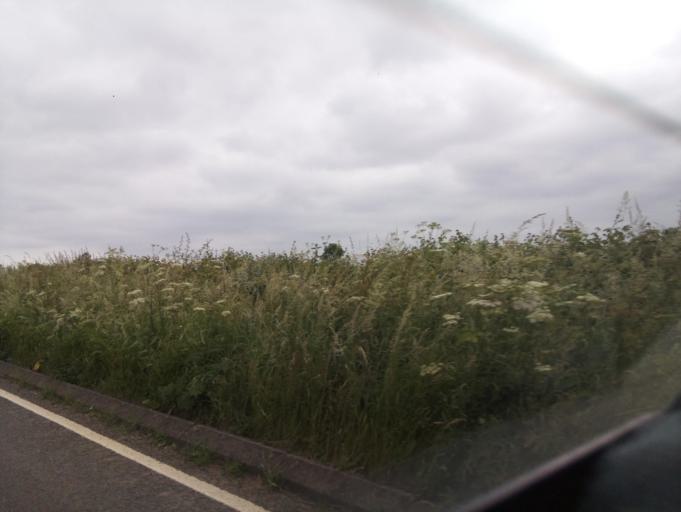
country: GB
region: England
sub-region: Leicestershire
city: Melton Mowbray
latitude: 52.7191
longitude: -0.8319
